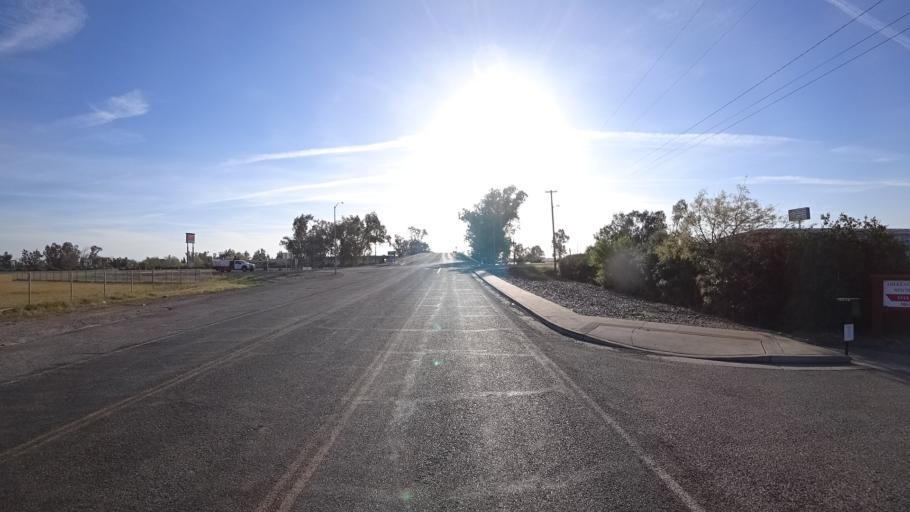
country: US
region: California
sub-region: Glenn County
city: Orland
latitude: 39.7403
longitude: -122.2080
